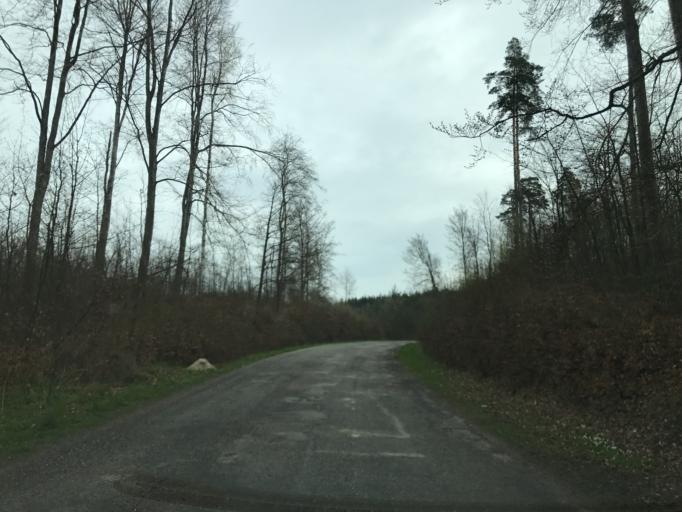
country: PL
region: Warmian-Masurian Voivodeship
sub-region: Powiat ostrodzki
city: Gierzwald
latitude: 53.6398
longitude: 20.0903
